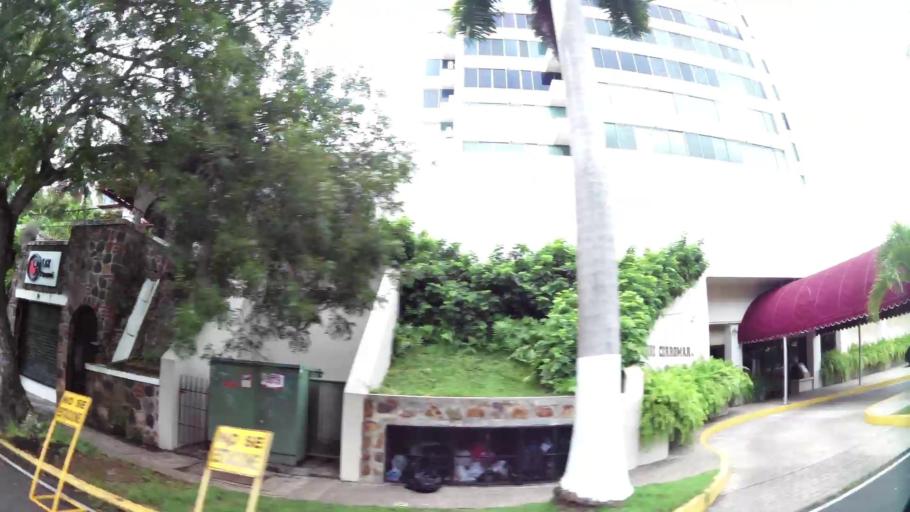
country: PA
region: Panama
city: Panama
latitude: 8.9778
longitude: -79.5288
